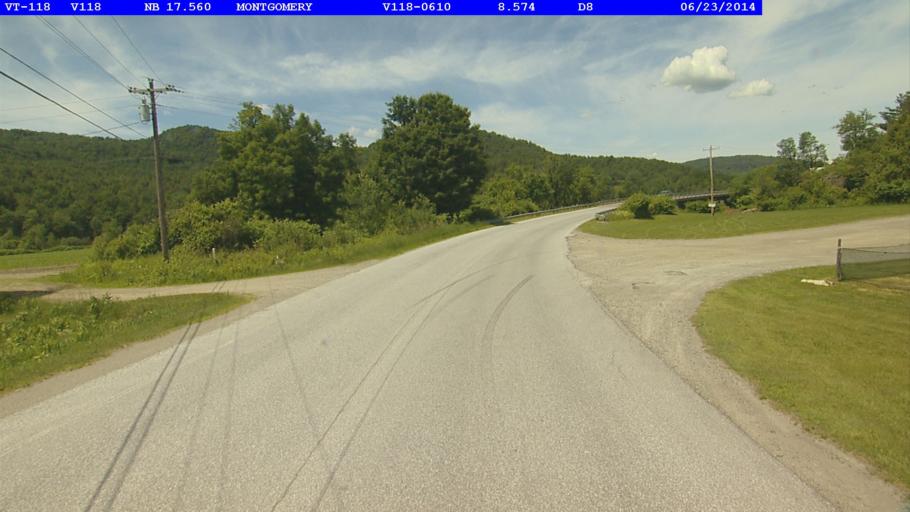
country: US
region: Vermont
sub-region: Franklin County
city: Richford
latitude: 44.9010
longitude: -72.6505
